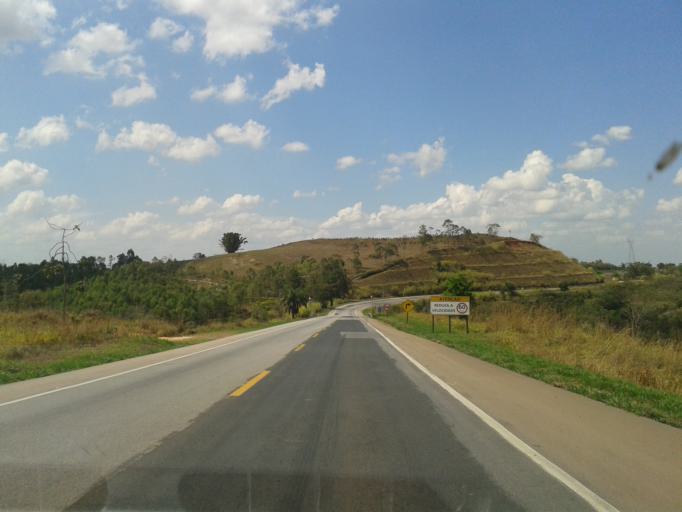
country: BR
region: Minas Gerais
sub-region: Campos Altos
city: Campos Altos
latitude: -19.7437
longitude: -45.9468
